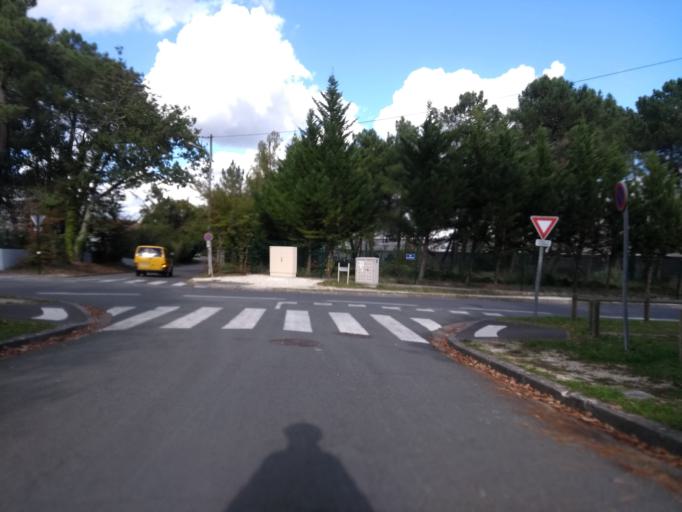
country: FR
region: Aquitaine
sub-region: Departement de la Gironde
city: Gradignan
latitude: 44.7816
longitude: -0.5990
